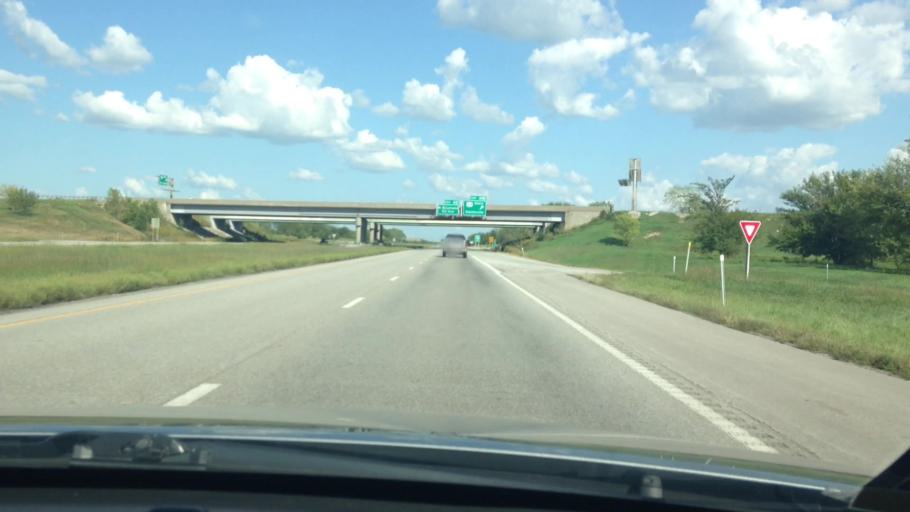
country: US
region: Missouri
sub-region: Clay County
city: Smithville
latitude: 39.3091
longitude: -94.5868
